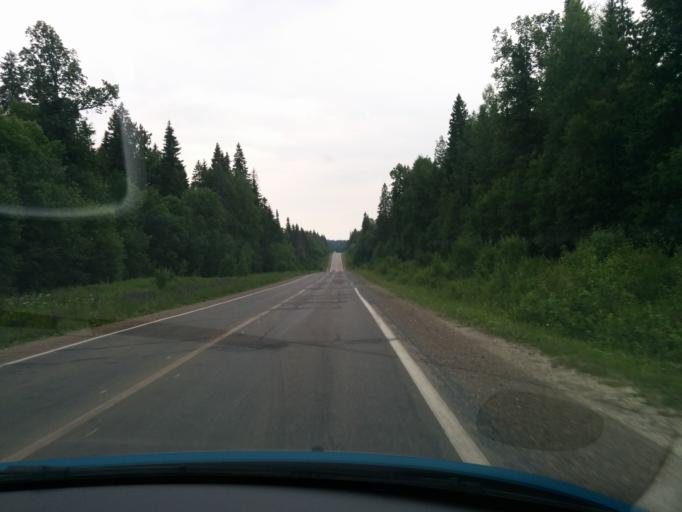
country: RU
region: Perm
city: Perm
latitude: 58.1888
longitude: 56.2171
